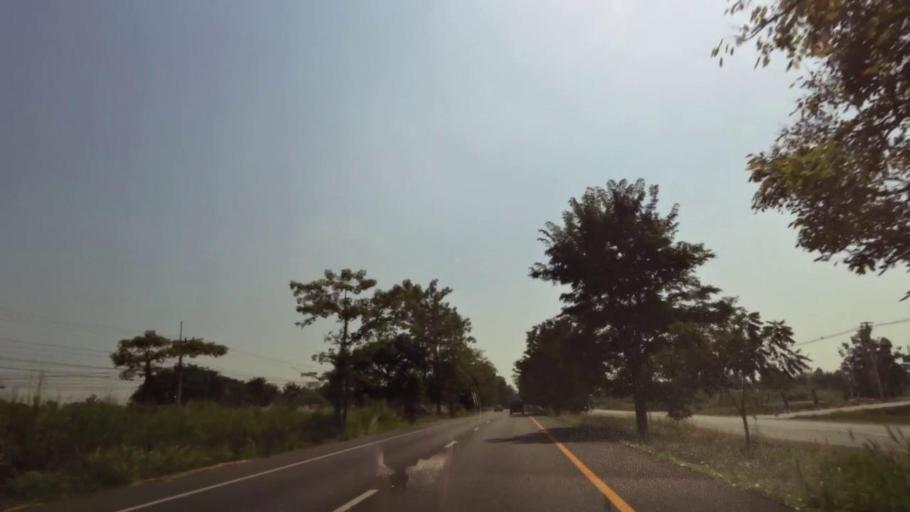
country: TH
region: Nakhon Sawan
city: Kao Liao
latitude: 15.9694
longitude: 100.1195
